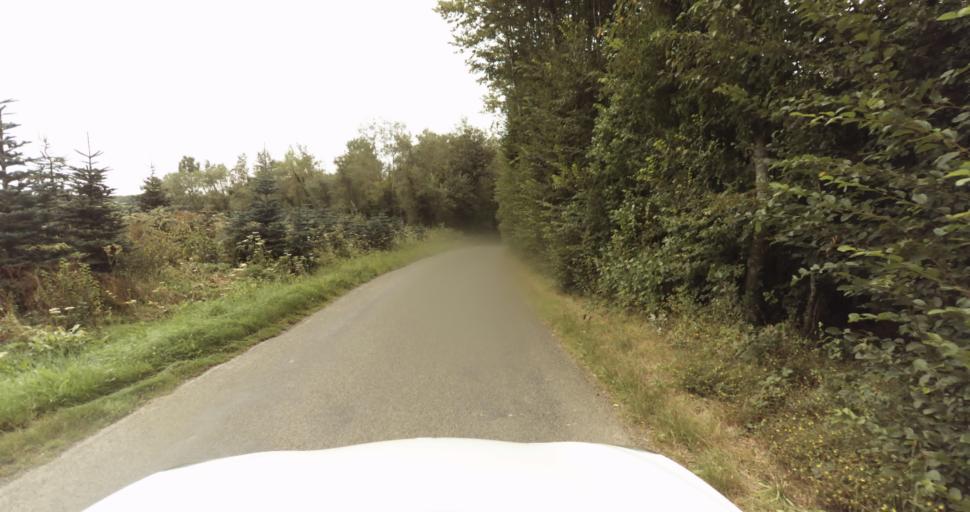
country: FR
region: Haute-Normandie
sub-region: Departement de l'Eure
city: Saint-Sebastien-de-Morsent
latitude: 49.0316
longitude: 1.0630
